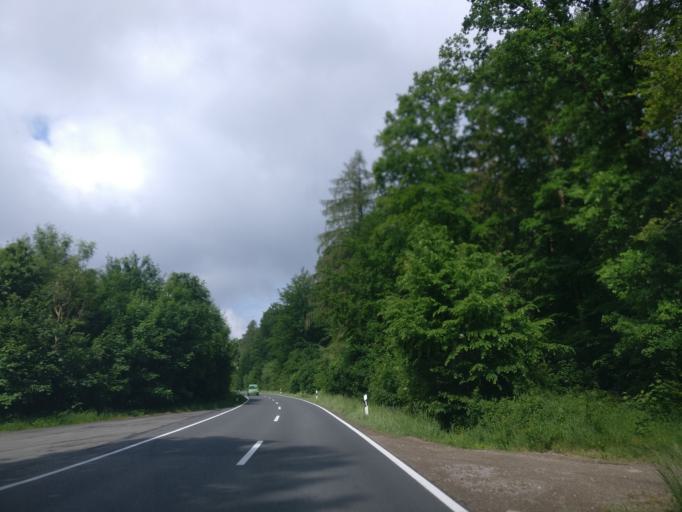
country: DE
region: Lower Saxony
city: Hannoversch Munden
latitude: 51.4043
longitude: 9.7024
